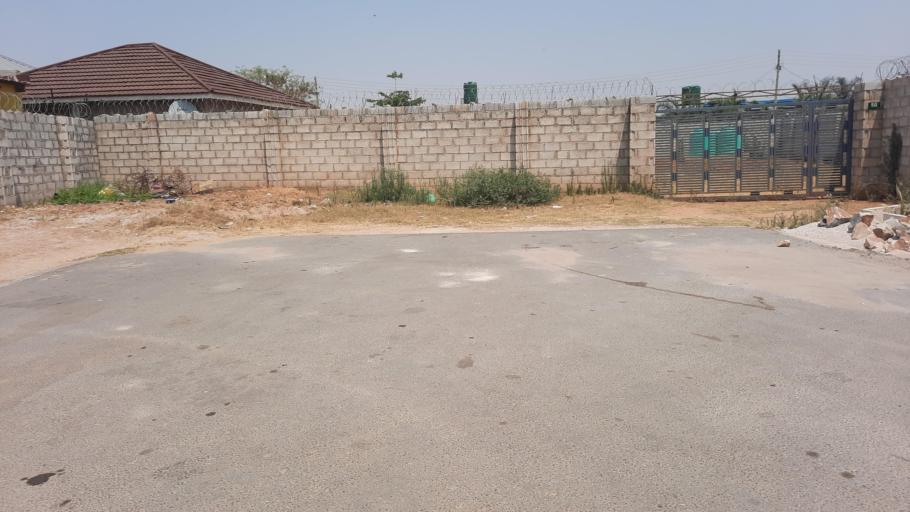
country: ZM
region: Lusaka
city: Lusaka
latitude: -15.3955
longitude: 28.3848
